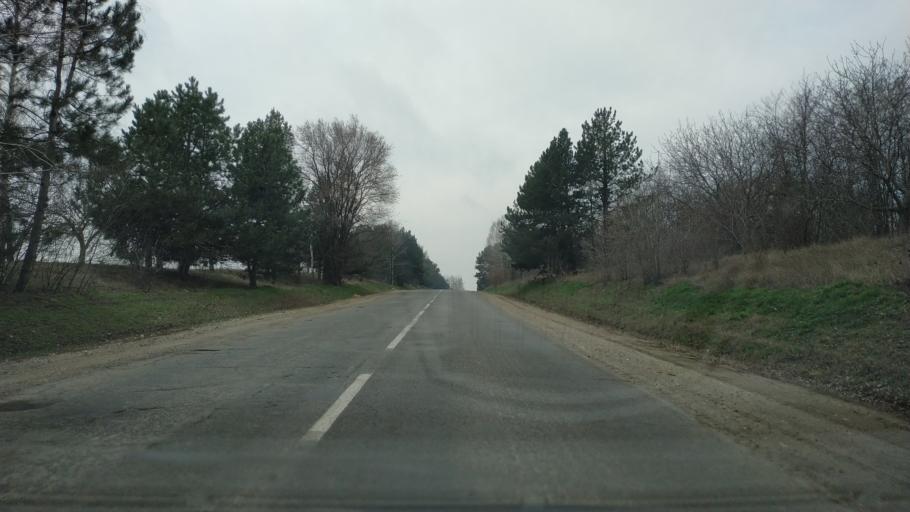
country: MD
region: Cahul
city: Cahul
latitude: 45.9386
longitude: 28.2887
